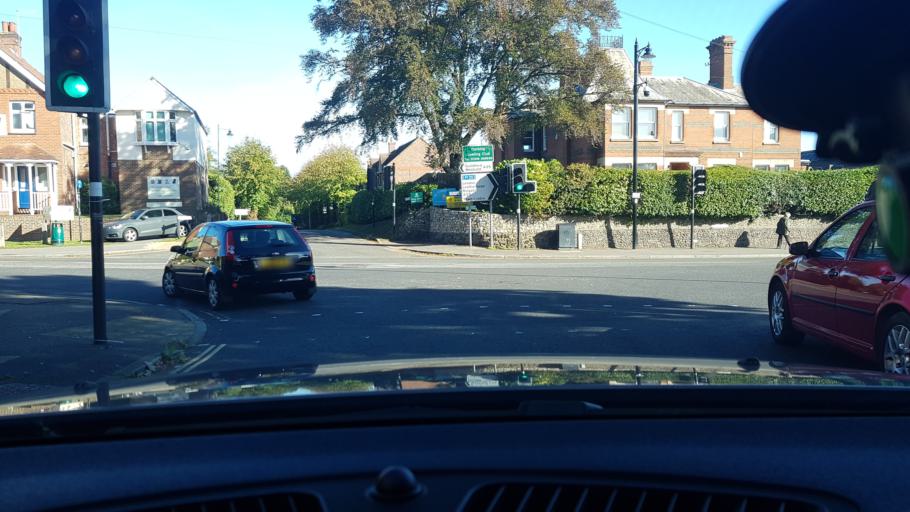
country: GB
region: England
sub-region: Surrey
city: Dorking
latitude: 51.2315
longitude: -0.3382
